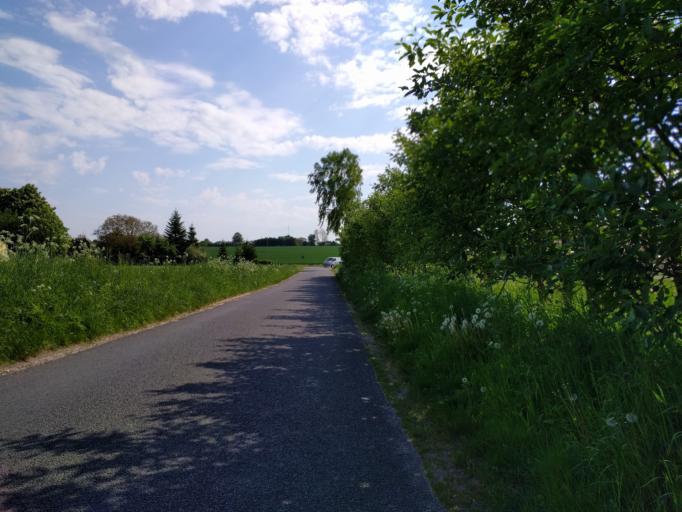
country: DK
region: South Denmark
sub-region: Kerteminde Kommune
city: Munkebo
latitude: 55.4716
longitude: 10.5962
